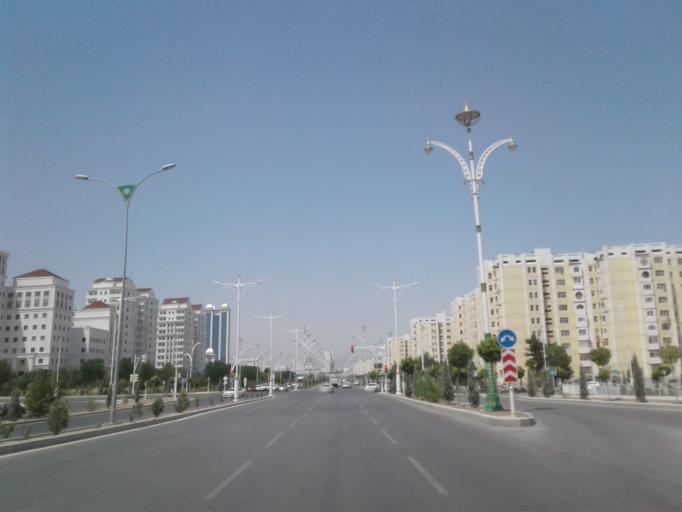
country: TM
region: Ahal
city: Ashgabat
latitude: 37.8954
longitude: 58.3982
